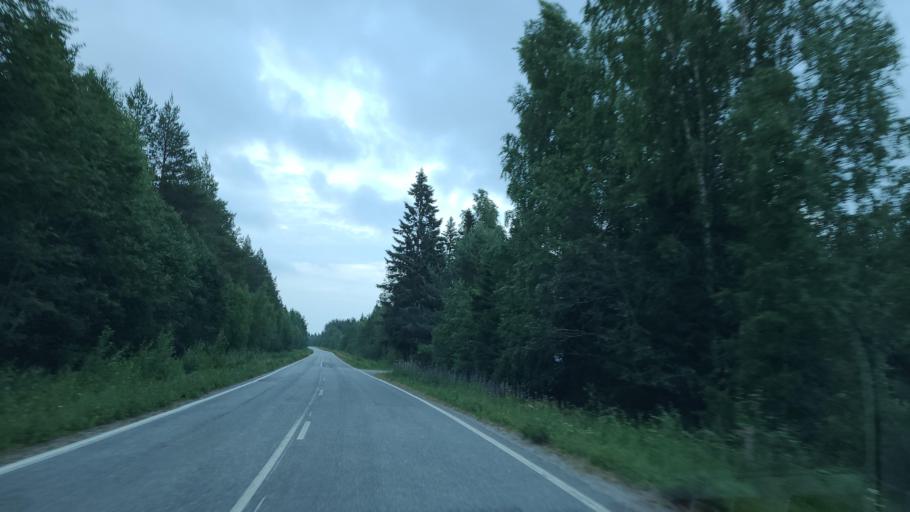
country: FI
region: Ostrobothnia
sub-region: Vaasa
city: Replot
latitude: 63.2736
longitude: 21.1427
